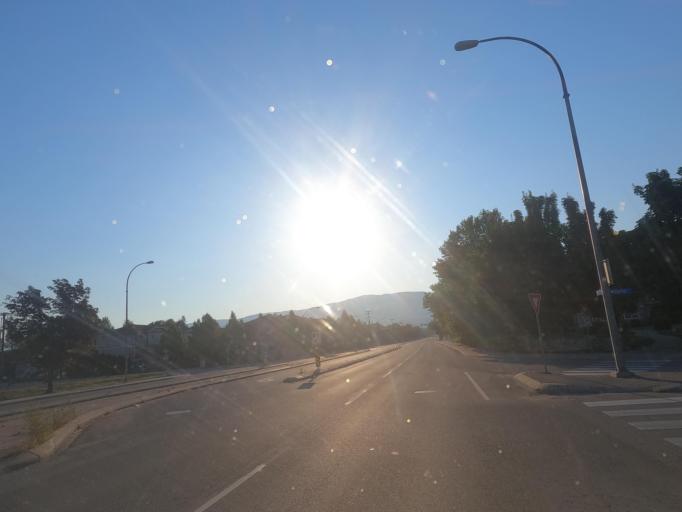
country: CA
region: British Columbia
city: Kelowna
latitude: 49.8889
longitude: -119.4177
